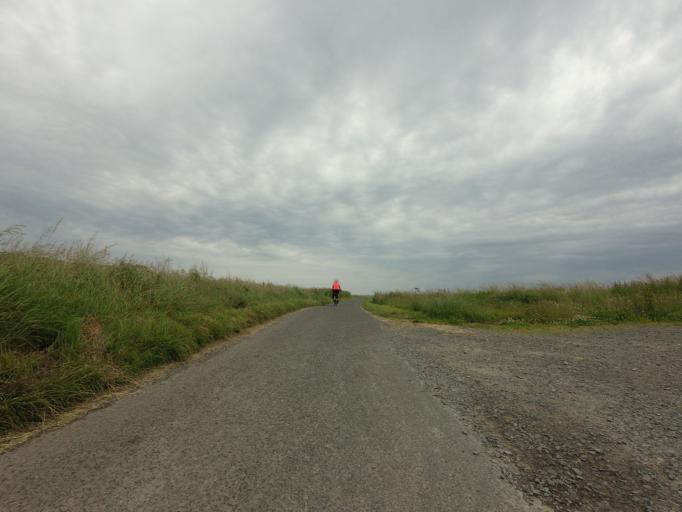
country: GB
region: Scotland
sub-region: Aberdeenshire
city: Whitehills
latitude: 57.6771
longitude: -2.5683
